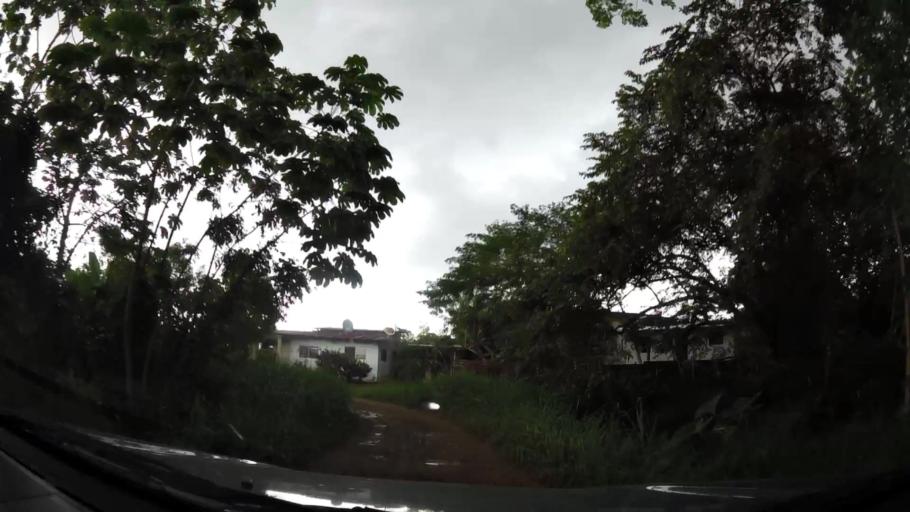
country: PA
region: Panama
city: San Miguelito
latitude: 9.0560
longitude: -79.4432
